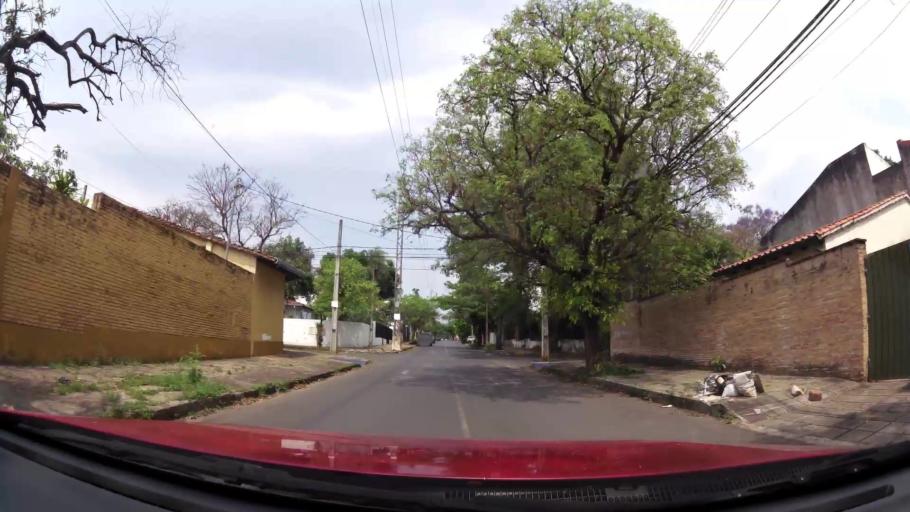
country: PY
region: Asuncion
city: Asuncion
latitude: -25.2881
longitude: -57.5843
